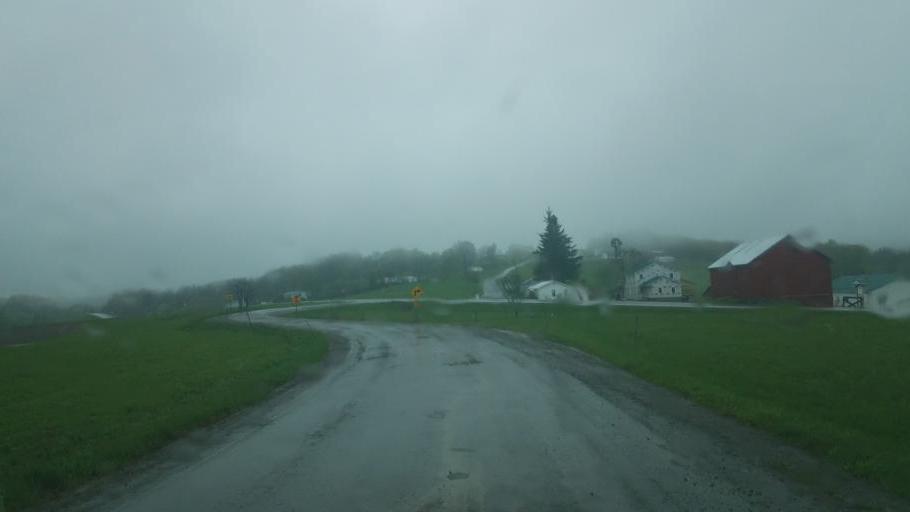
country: US
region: New York
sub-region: Steuben County
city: Canisteo
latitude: 42.1080
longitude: -77.5278
